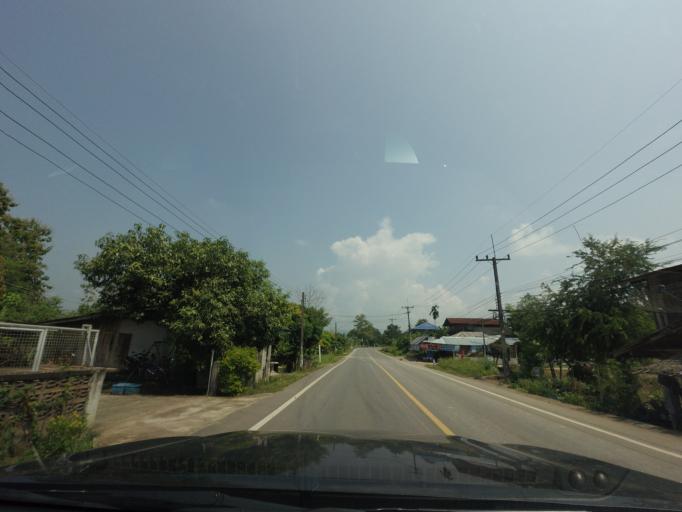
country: TH
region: Nan
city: Nan
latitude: 18.8619
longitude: 100.8264
